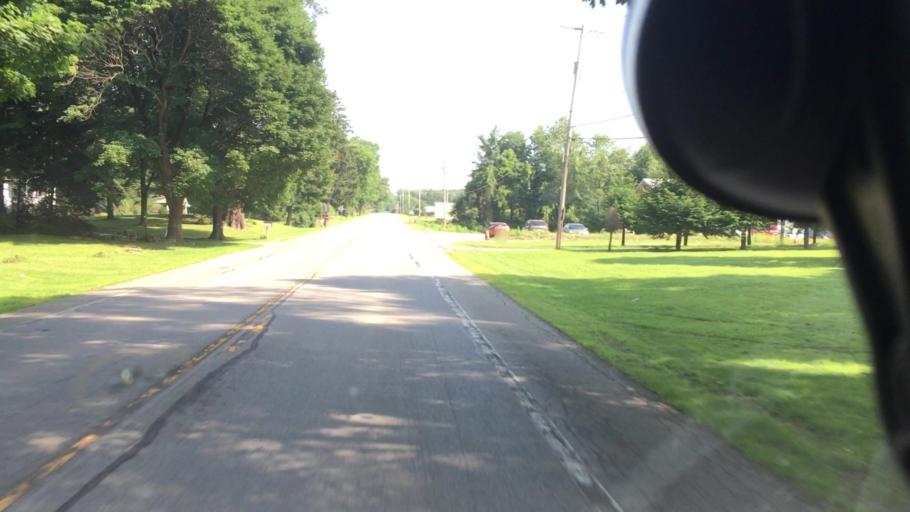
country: US
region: Pennsylvania
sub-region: Butler County
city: Slippery Rock
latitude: 41.0292
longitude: -80.1913
